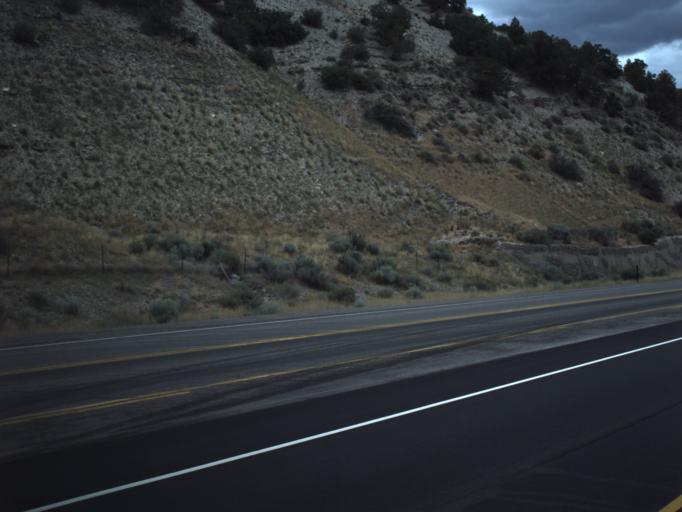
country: US
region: Utah
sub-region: Utah County
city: Mapleton
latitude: 39.9517
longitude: -111.2798
